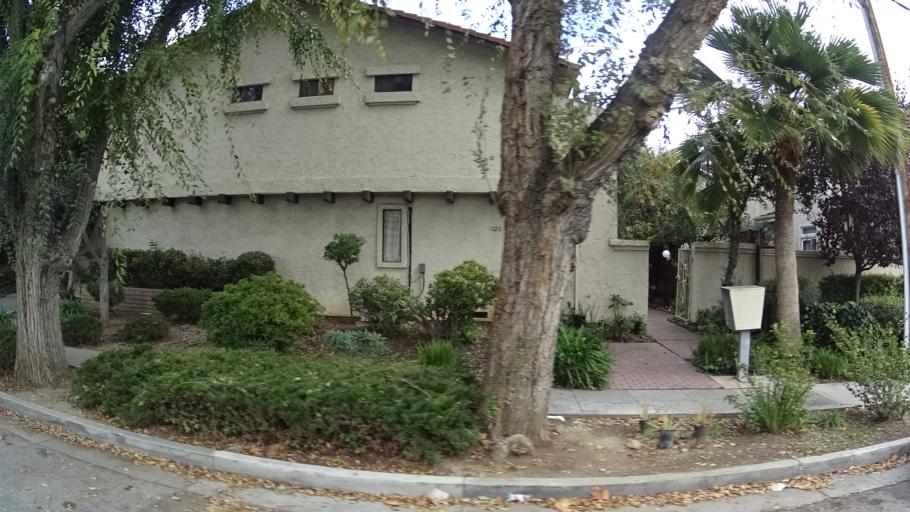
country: US
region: California
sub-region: Santa Clara County
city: Sunnyvale
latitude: 37.3538
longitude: -122.0010
